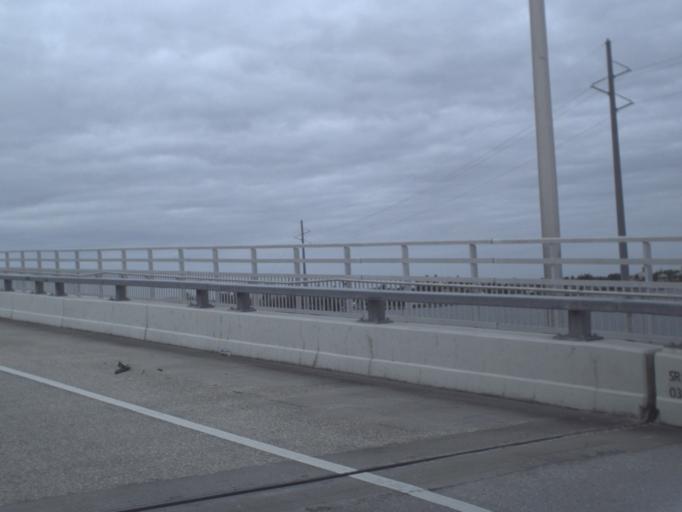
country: US
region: Florida
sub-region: Collier County
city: Marco
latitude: 25.9656
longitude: -81.7090
